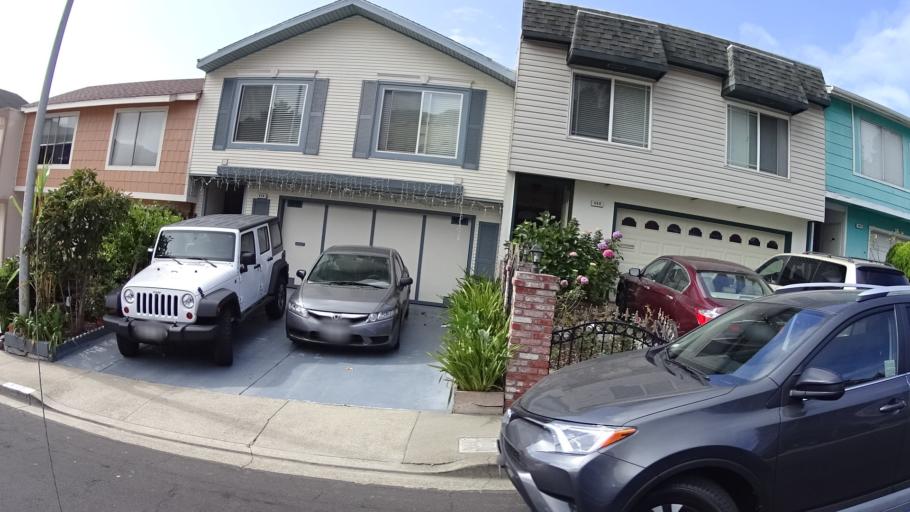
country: US
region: California
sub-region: San Mateo County
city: Daly City
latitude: 37.6958
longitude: -122.4579
